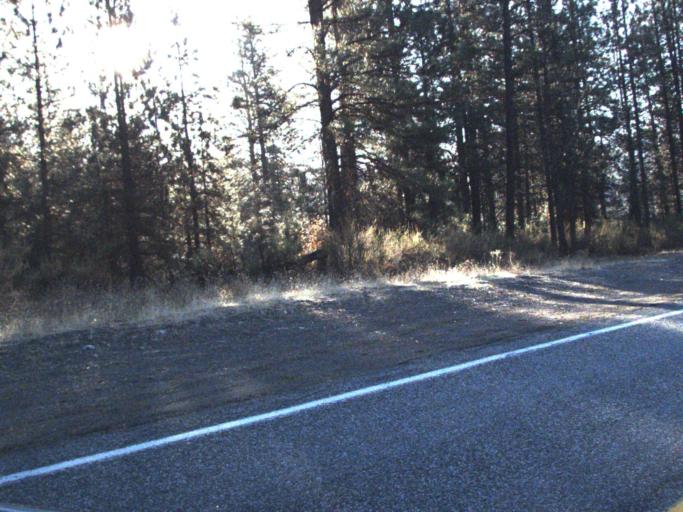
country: US
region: Washington
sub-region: Okanogan County
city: Coulee Dam
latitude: 48.0502
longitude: -118.6688
